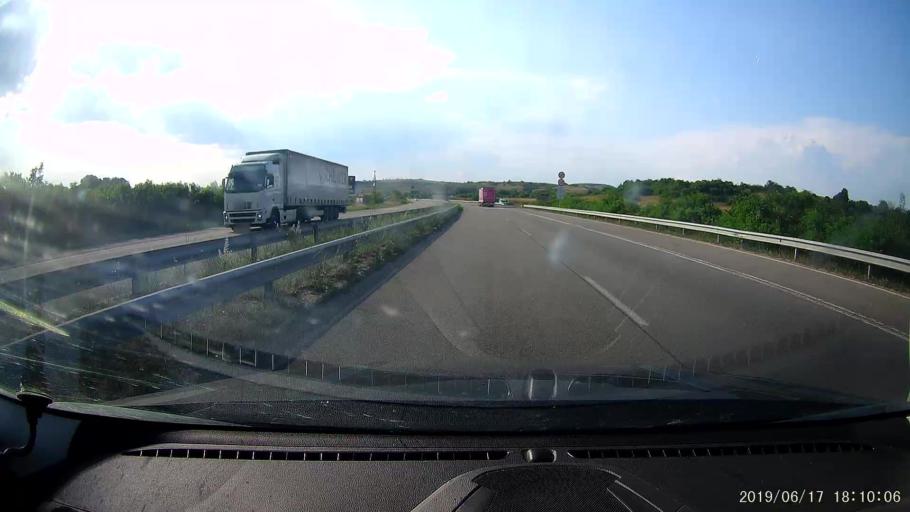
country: BG
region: Khaskovo
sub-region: Obshtina Lyubimets
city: Lyubimets
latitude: 41.8701
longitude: 26.0832
